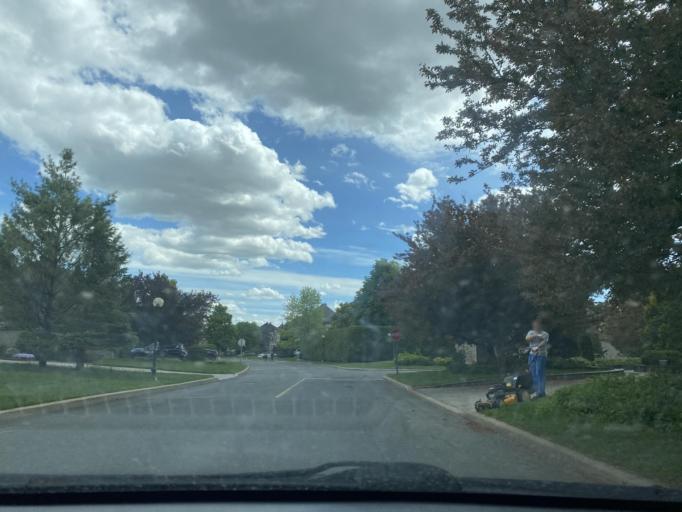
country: CA
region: Quebec
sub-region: Monteregie
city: Carignan
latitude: 45.4698
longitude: -73.2958
